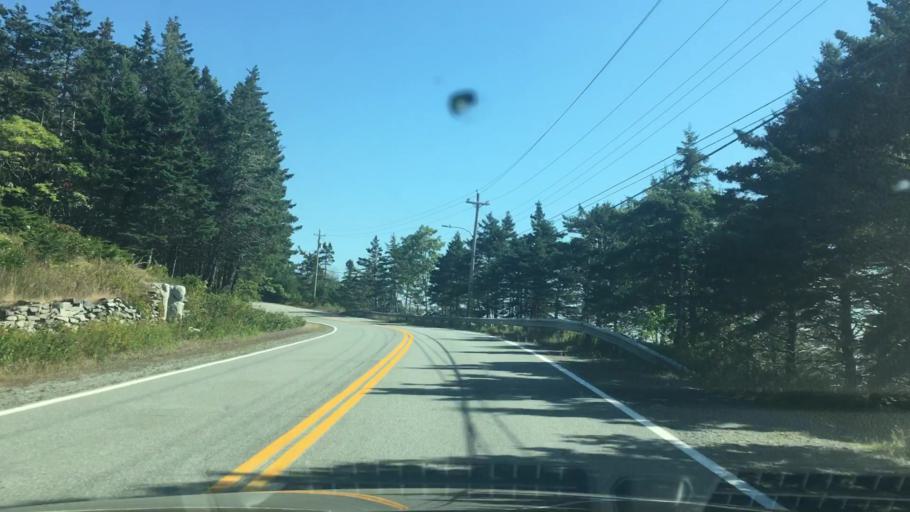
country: CA
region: Nova Scotia
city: New Glasgow
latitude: 44.8234
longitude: -62.6318
